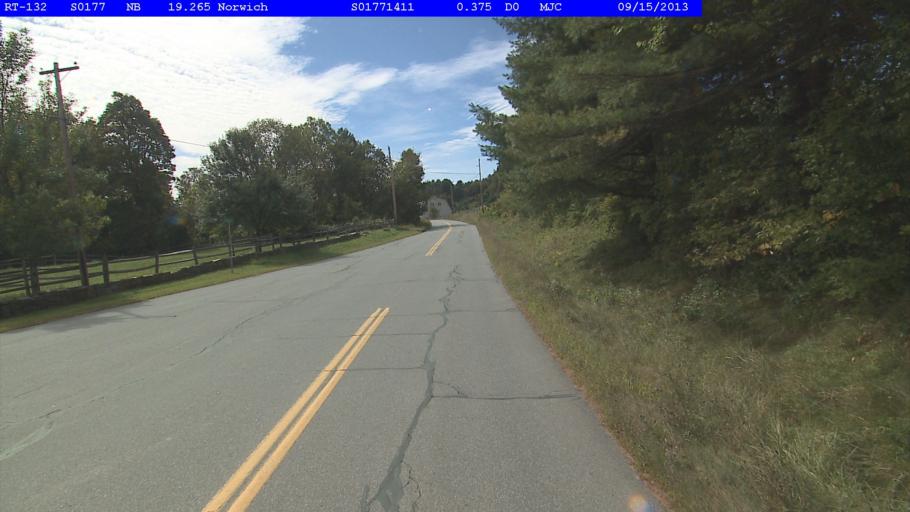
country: US
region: New Hampshire
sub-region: Grafton County
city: Hanover
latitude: 43.7814
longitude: -72.2584
